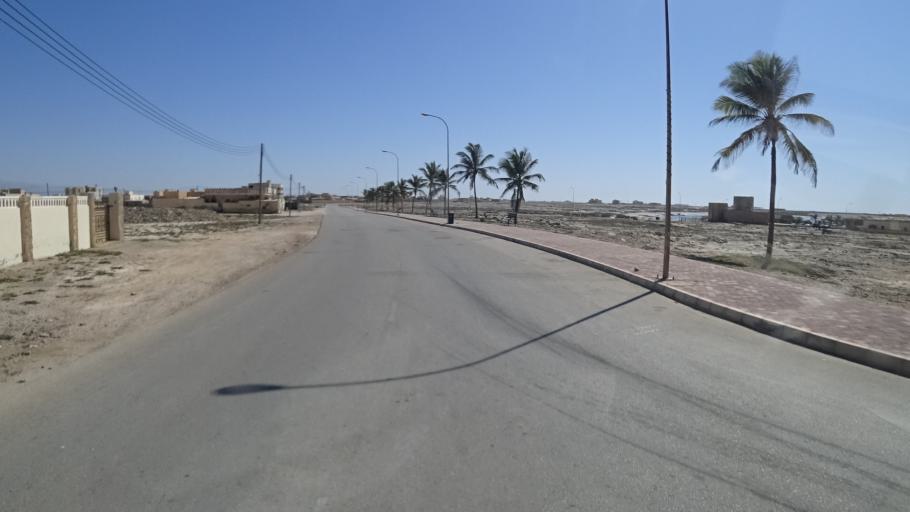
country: OM
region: Zufar
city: Salalah
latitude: 16.9771
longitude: 54.6903
